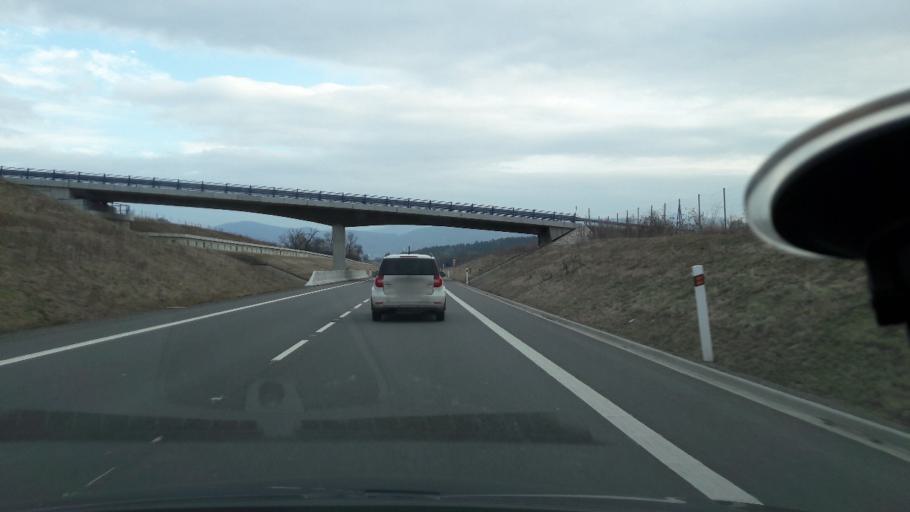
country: SK
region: Banskobystricky
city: Ziar nad Hronom
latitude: 48.6038
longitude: 18.8167
